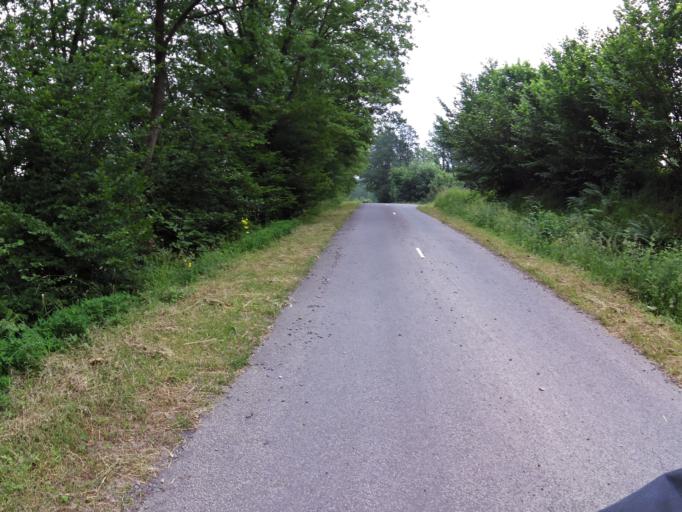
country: FR
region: Champagne-Ardenne
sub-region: Departement des Ardennes
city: Fumay
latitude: 49.9789
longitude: 4.6748
